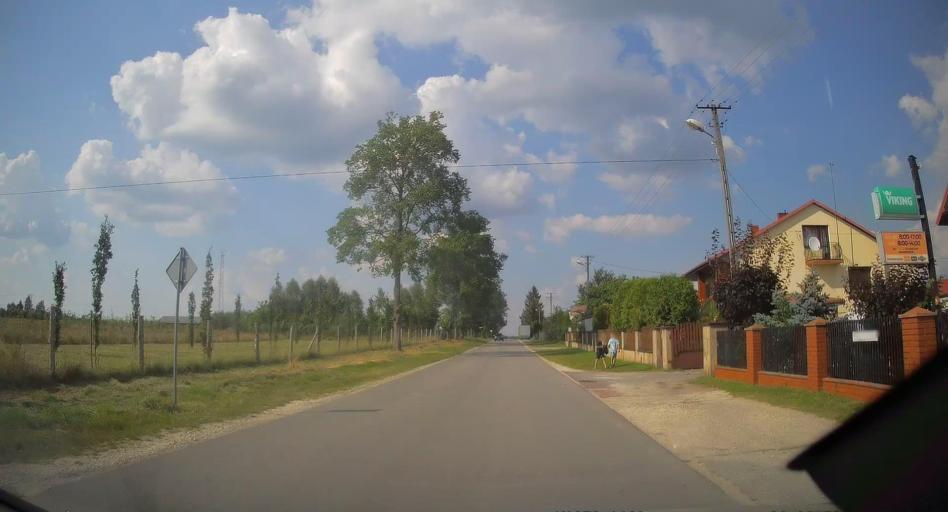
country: PL
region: Swietokrzyskie
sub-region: Powiat konecki
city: Radoszyce
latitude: 51.0815
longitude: 20.2578
